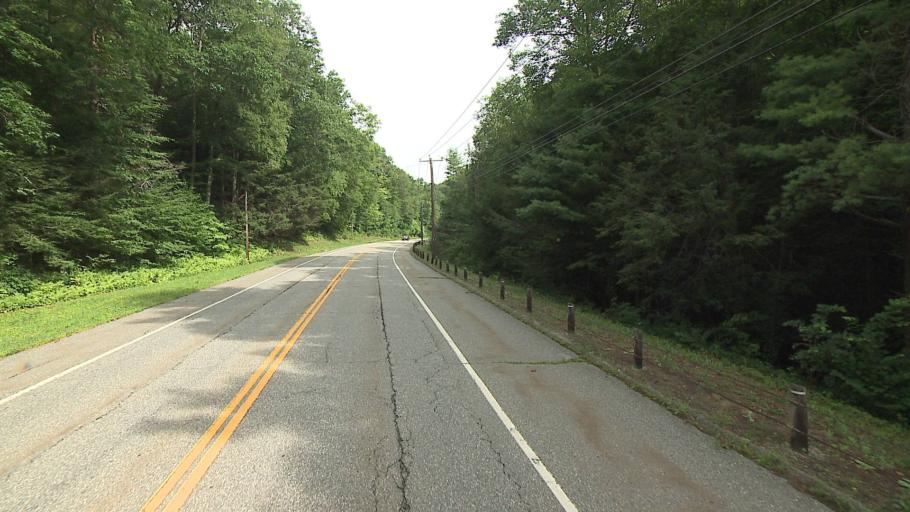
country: US
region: Connecticut
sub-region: Litchfield County
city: New Preston
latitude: 41.6645
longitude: -73.3211
